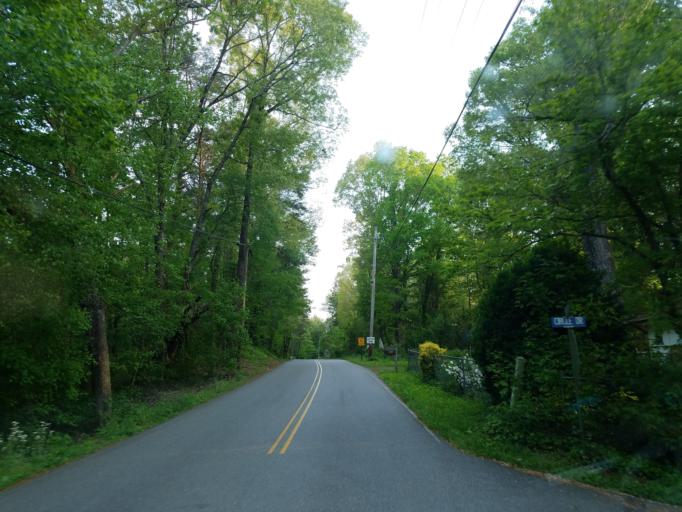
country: US
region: Georgia
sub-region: Fannin County
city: Blue Ridge
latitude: 34.8716
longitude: -84.2482
